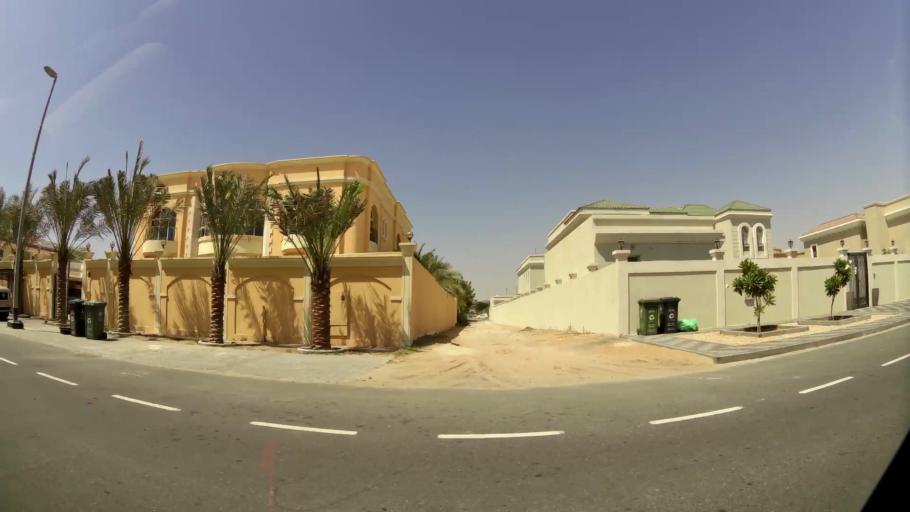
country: AE
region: Dubai
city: Dubai
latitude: 25.1045
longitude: 55.2090
